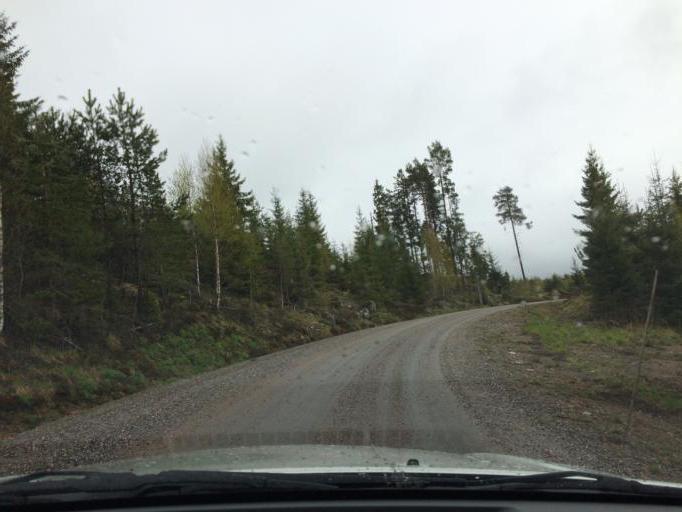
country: SE
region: OErebro
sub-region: Hallefors Kommun
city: Haellefors
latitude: 60.0186
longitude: 14.5864
